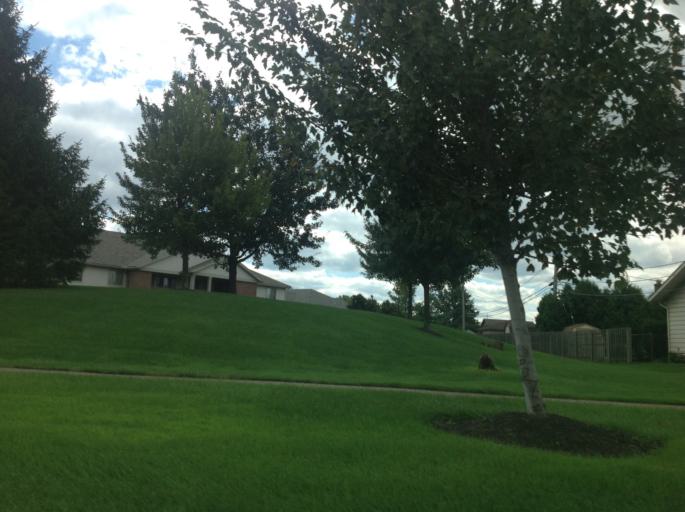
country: US
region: Ohio
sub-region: Cuyahoga County
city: Brooklyn
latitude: 41.4298
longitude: -81.7426
